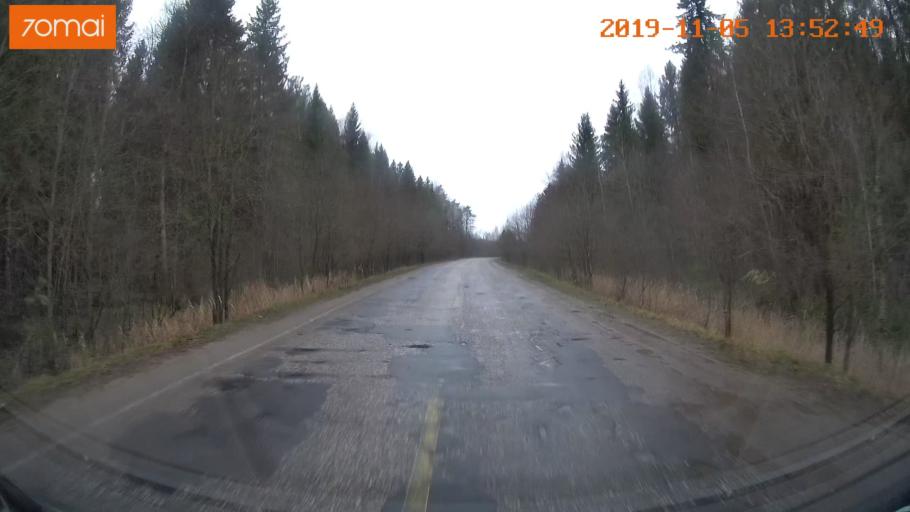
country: RU
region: Ivanovo
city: Kaminskiy
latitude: 57.0292
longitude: 41.3804
